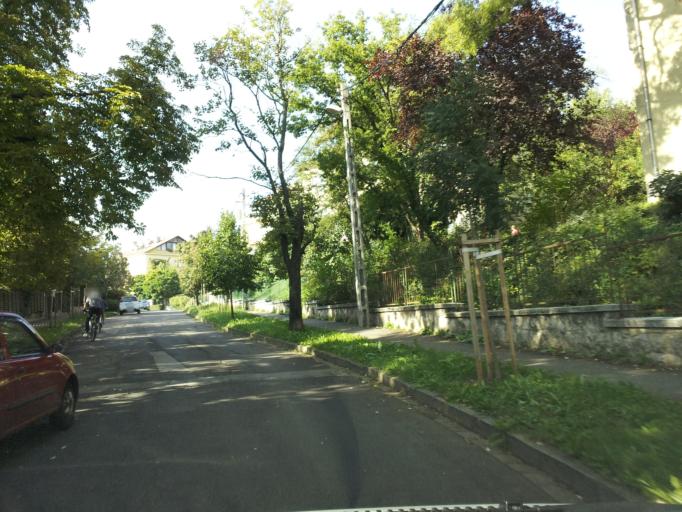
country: HU
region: Budapest
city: Budapest II. keruelet
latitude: 47.5144
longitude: 19.0096
